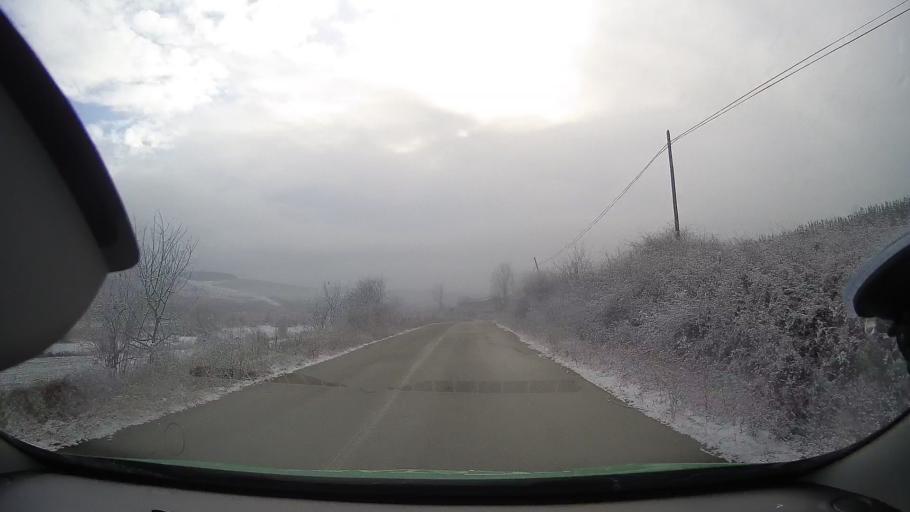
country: RO
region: Mures
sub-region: Comuna Chetani
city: Chetani
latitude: 46.4212
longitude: 24.0153
